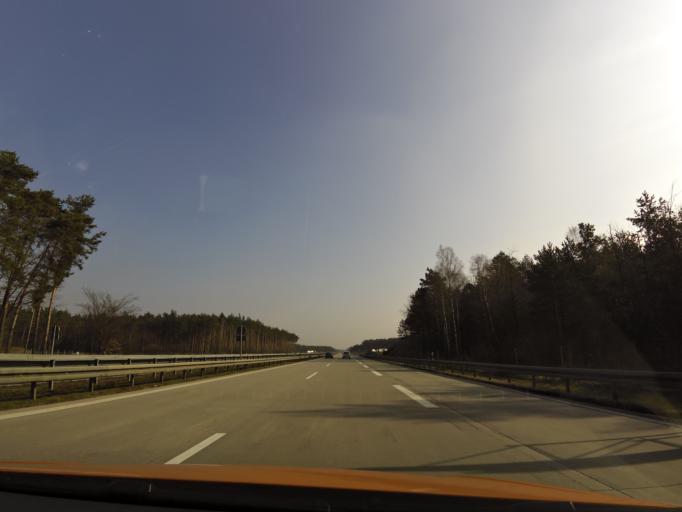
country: DE
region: Brandenburg
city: Briesen
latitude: 52.3370
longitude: 14.2142
